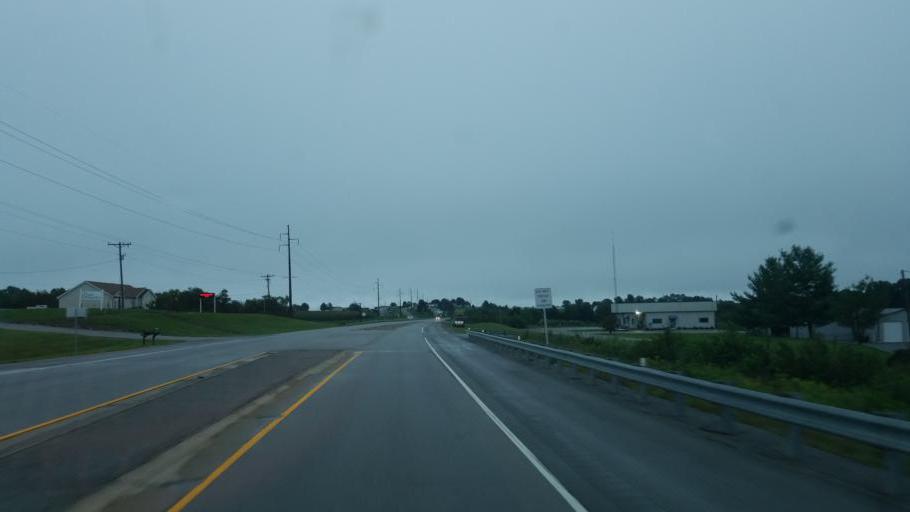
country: US
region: Kentucky
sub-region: Fleming County
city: Flemingsburg
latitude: 38.4122
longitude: -83.7382
